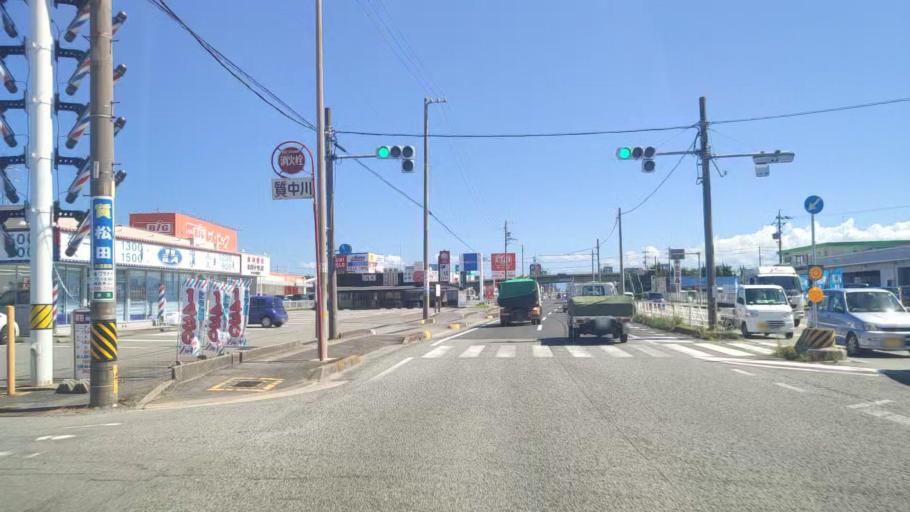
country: JP
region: Mie
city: Tsu-shi
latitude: 34.6854
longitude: 136.5178
